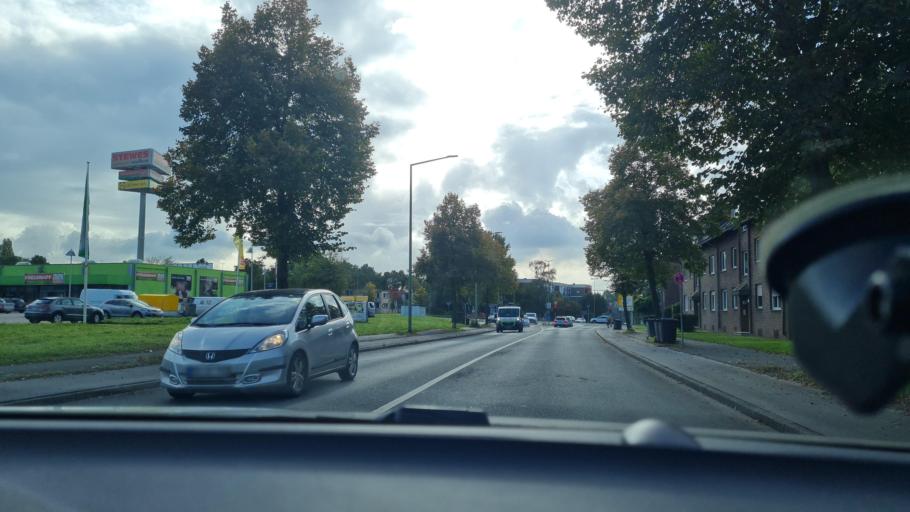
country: DE
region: North Rhine-Westphalia
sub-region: Regierungsbezirk Dusseldorf
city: Dinslaken
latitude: 51.5287
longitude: 6.7546
